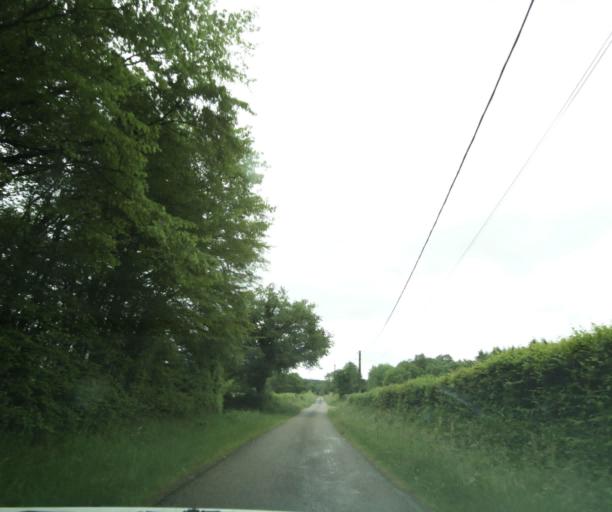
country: FR
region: Bourgogne
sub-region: Departement de Saone-et-Loire
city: Charolles
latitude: 46.5065
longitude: 4.2920
